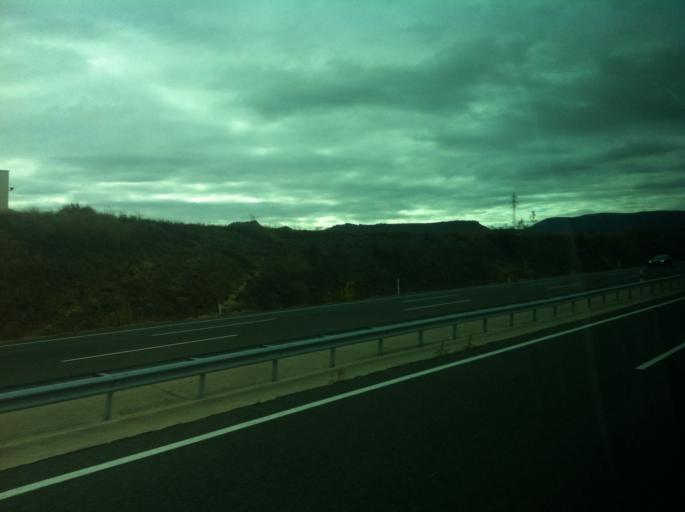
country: ES
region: Castille and Leon
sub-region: Provincia de Burgos
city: Miranda de Ebro
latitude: 42.6943
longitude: -2.9842
